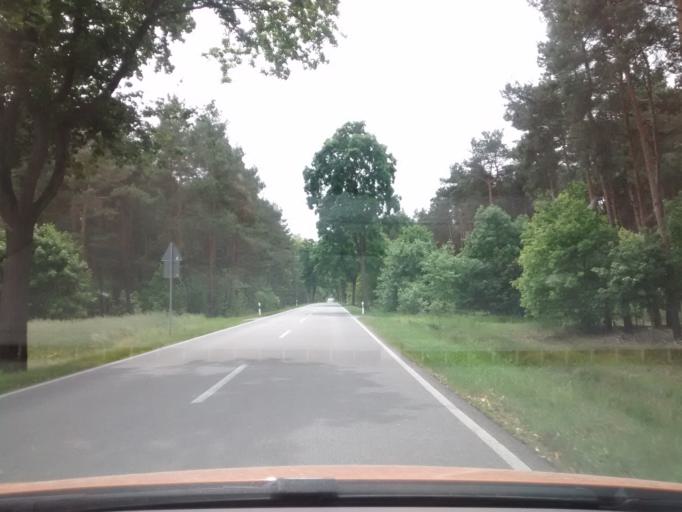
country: DE
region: Saxony-Anhalt
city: Holzdorf
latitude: 51.8891
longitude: 13.1418
